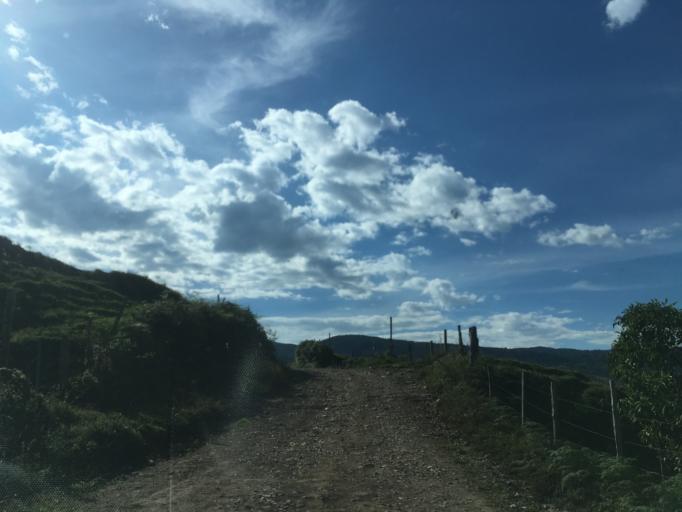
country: CO
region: Santander
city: Oiba
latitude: 6.1407
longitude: -73.1906
